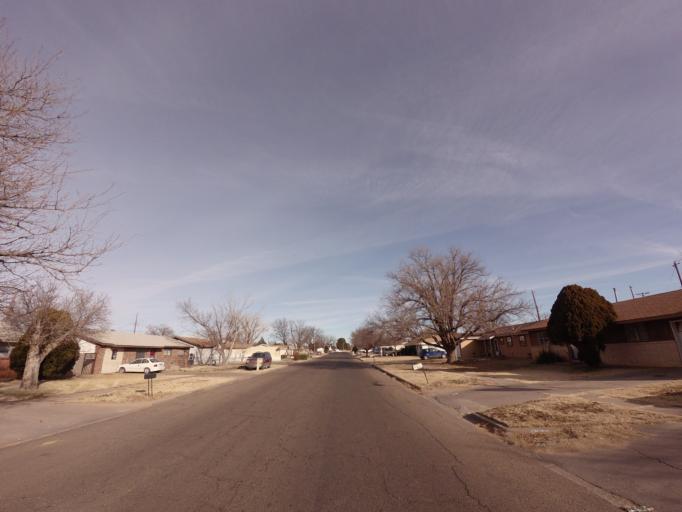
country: US
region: New Mexico
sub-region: Curry County
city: Clovis
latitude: 34.4169
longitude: -103.2229
